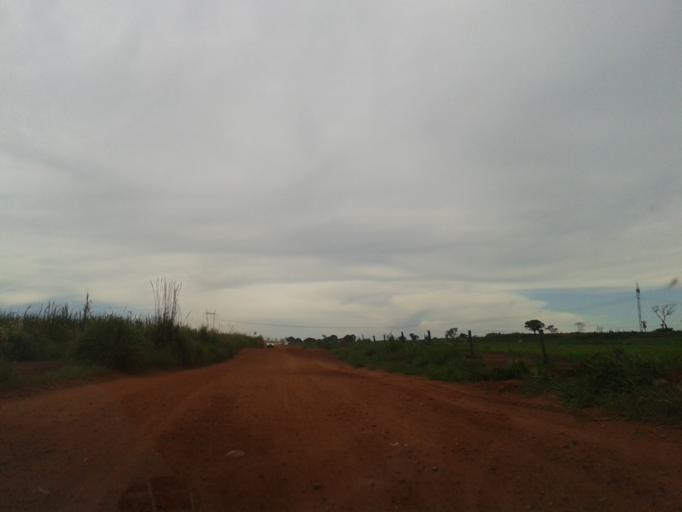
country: BR
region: Minas Gerais
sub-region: Santa Vitoria
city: Santa Vitoria
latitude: -19.0537
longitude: -50.4792
